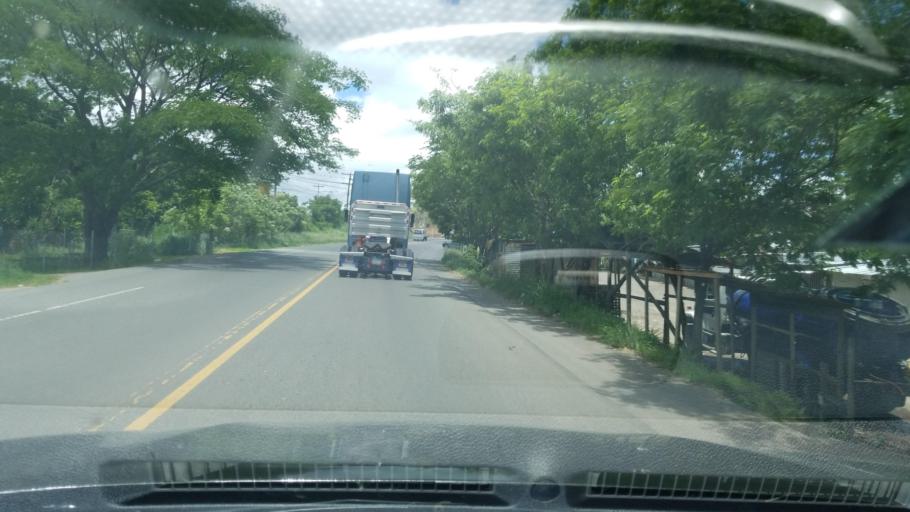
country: HN
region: Francisco Morazan
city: Rio Abajo
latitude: 14.1536
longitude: -87.2049
